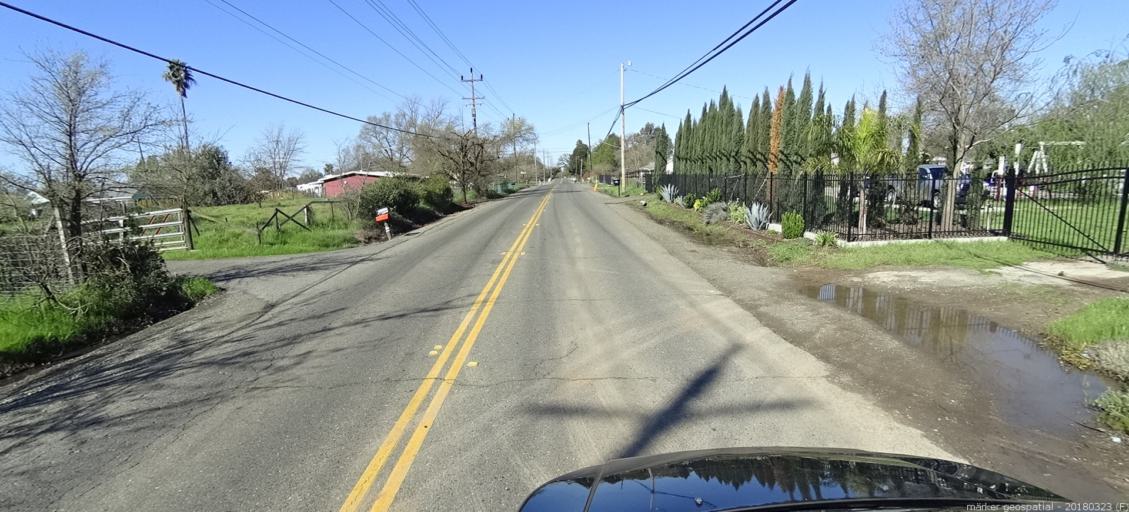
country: US
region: California
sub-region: Sacramento County
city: Rio Linda
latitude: 38.6979
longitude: -121.4138
